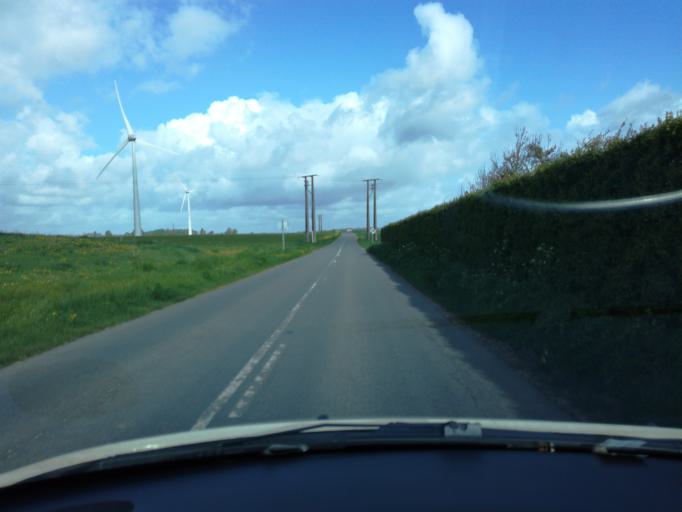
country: FR
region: Picardie
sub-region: Departement de la Somme
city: Beaucamps-le-Vieux
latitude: 49.9009
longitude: 1.8191
